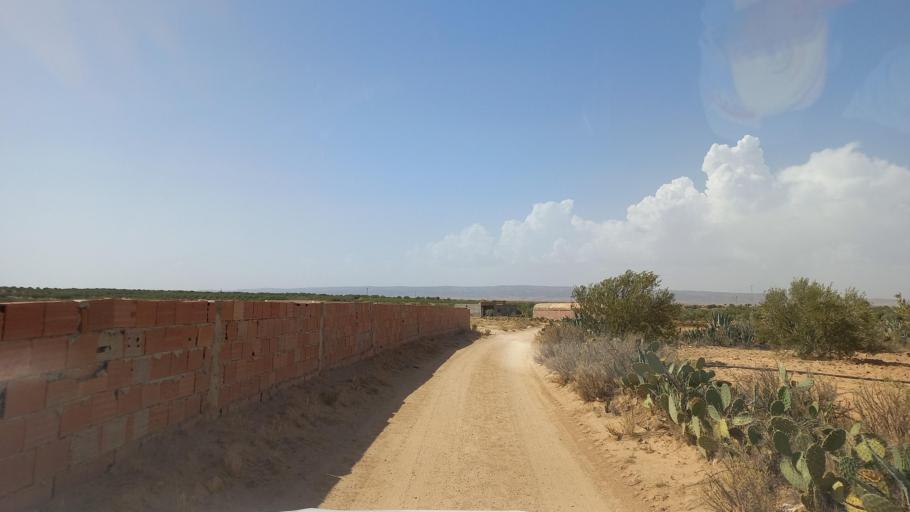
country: TN
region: Al Qasrayn
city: Kasserine
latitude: 35.2100
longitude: 9.0379
